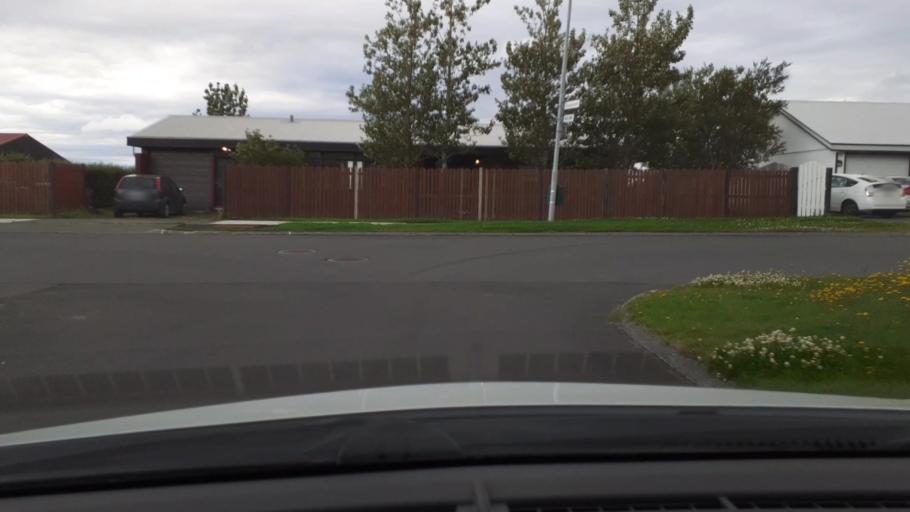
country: IS
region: Capital Region
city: Reykjavik
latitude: 64.2395
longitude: -21.8349
